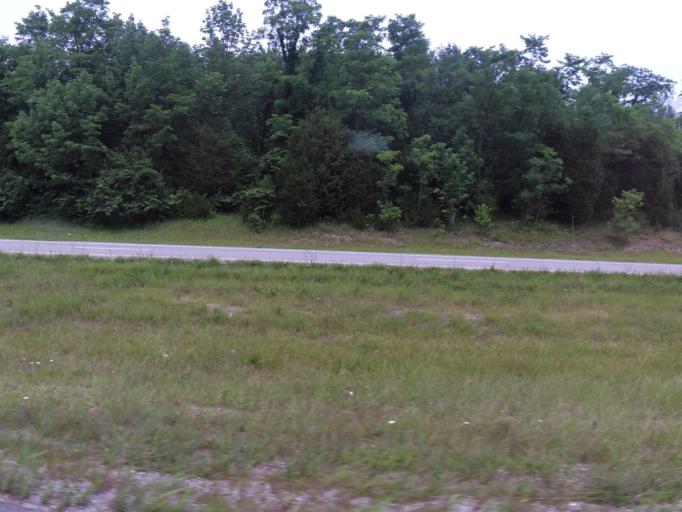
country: US
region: Ohio
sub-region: Warren County
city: Waynesville
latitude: 39.5022
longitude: -84.0197
